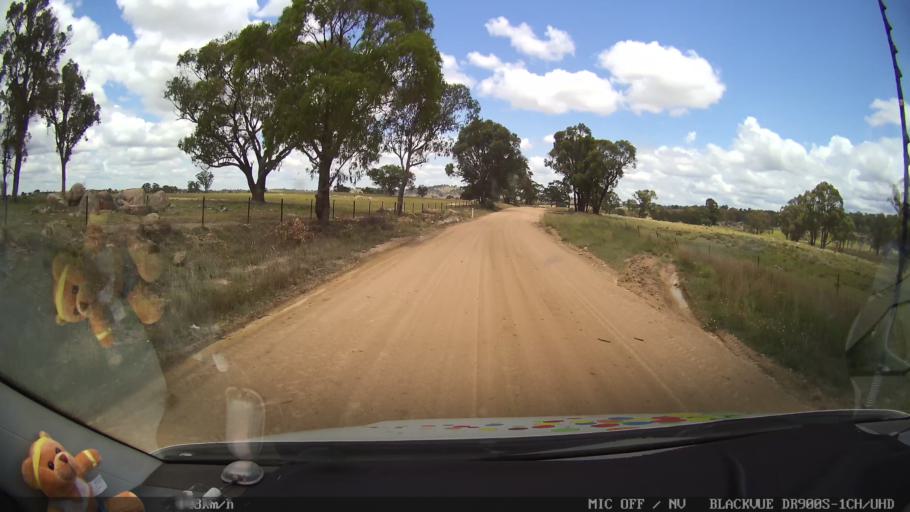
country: AU
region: New South Wales
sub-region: Glen Innes Severn
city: Glen Innes
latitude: -29.3486
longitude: 151.8877
